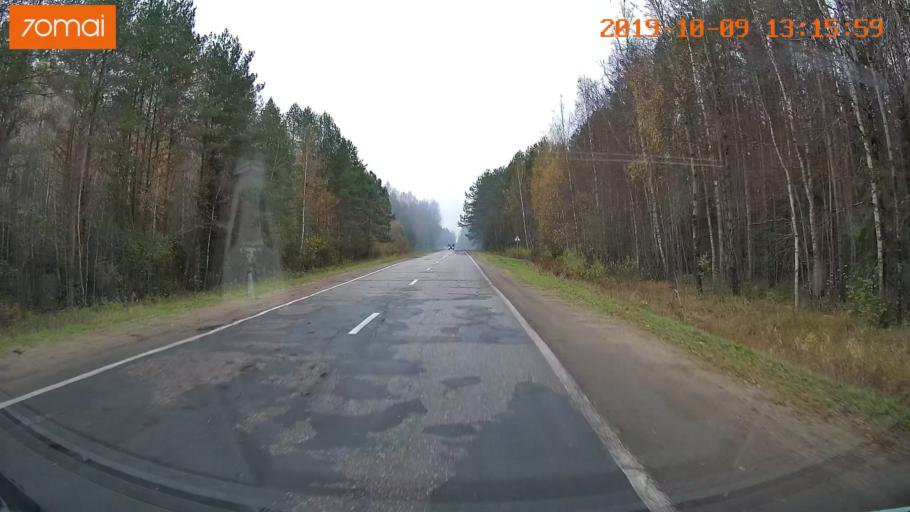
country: RU
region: Jaroslavl
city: Lyubim
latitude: 58.3642
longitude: 40.7599
